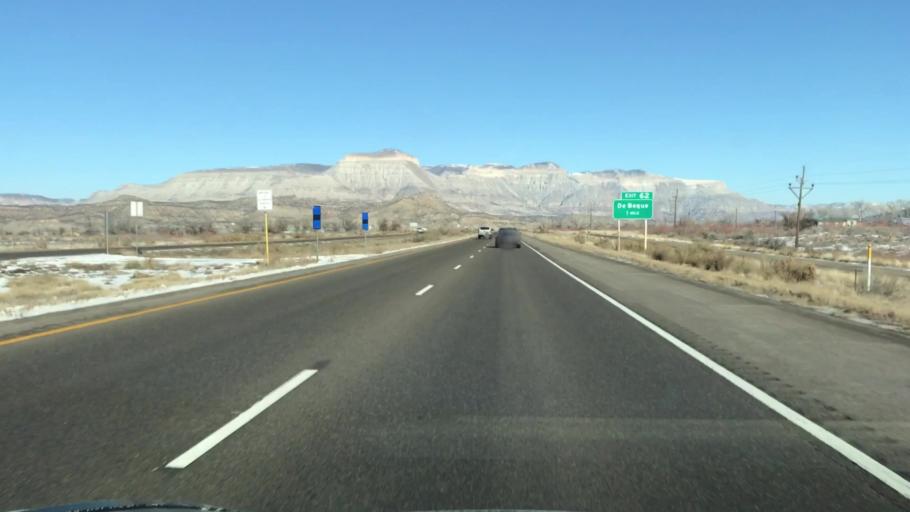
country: US
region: Colorado
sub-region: Garfield County
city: Parachute
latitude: 39.3071
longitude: -108.2165
